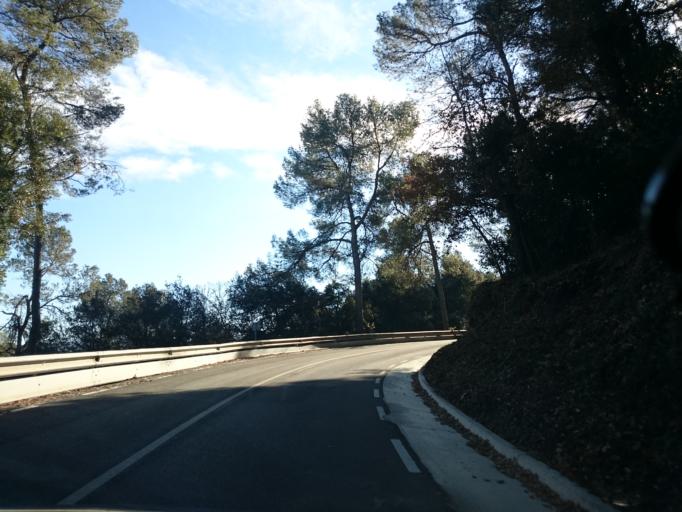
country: ES
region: Catalonia
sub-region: Provincia de Barcelona
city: Molins de Rei
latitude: 41.4306
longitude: 2.0551
